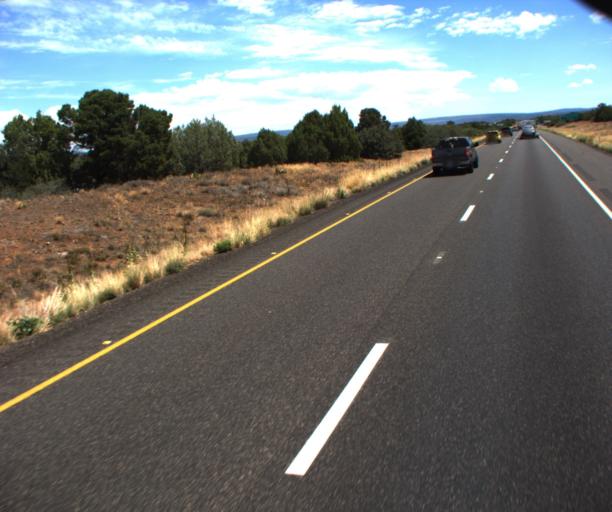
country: US
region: Arizona
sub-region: Yavapai County
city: Village of Oak Creek (Big Park)
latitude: 34.7457
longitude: -111.6828
